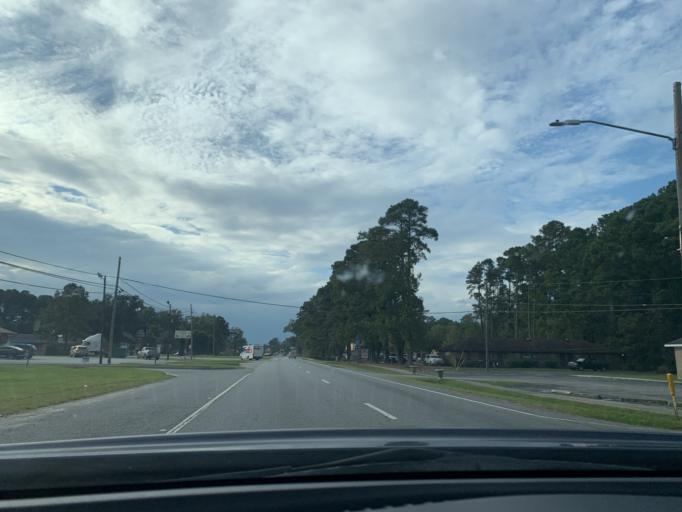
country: US
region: Georgia
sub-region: Chatham County
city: Pooler
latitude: 32.1183
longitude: -81.2551
